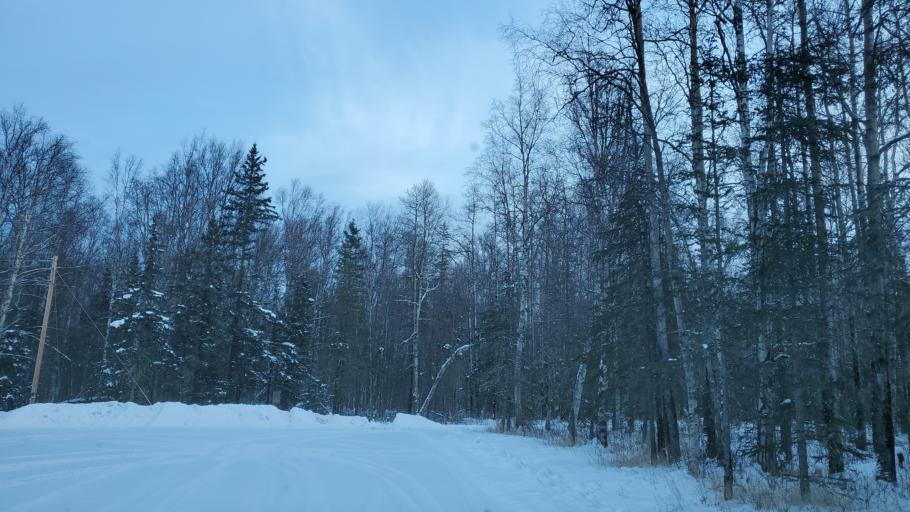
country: US
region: Alaska
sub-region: Matanuska-Susitna Borough
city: Lakes
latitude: 61.6716
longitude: -149.2778
